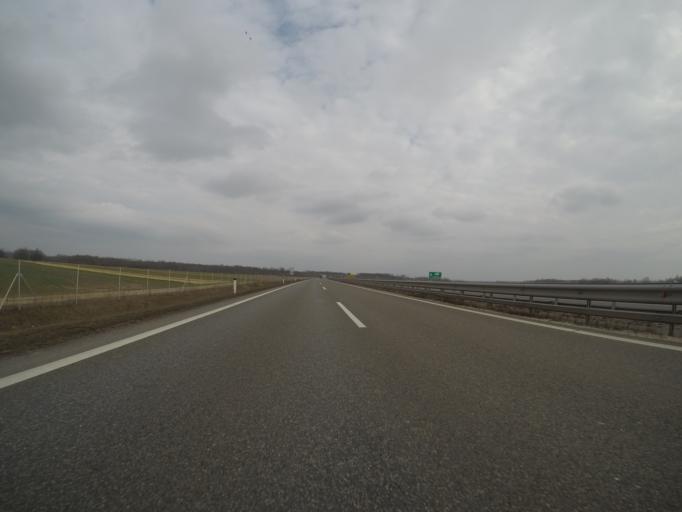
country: SI
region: Beltinci
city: Gancani
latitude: 46.6397
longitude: 16.2516
